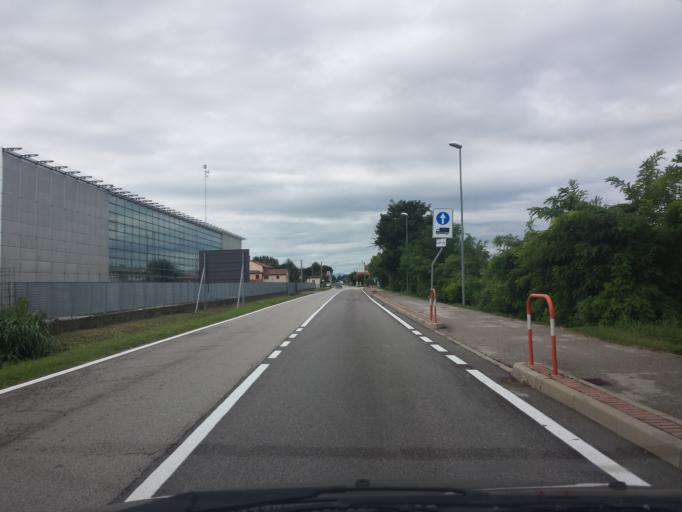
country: IT
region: Veneto
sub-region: Provincia di Padova
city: Galliera Veneta
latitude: 45.6714
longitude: 11.8147
